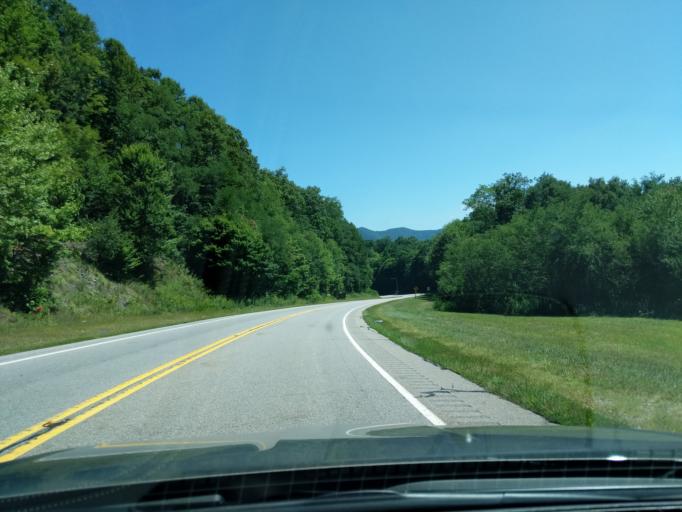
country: US
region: North Carolina
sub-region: Macon County
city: Franklin
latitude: 35.1311
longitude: -83.5189
